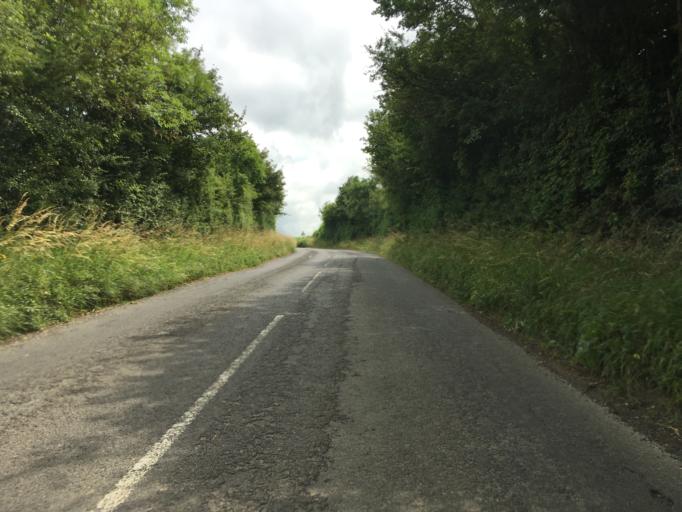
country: GB
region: England
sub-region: Oxfordshire
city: Charlbury
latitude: 51.8958
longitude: -1.5009
